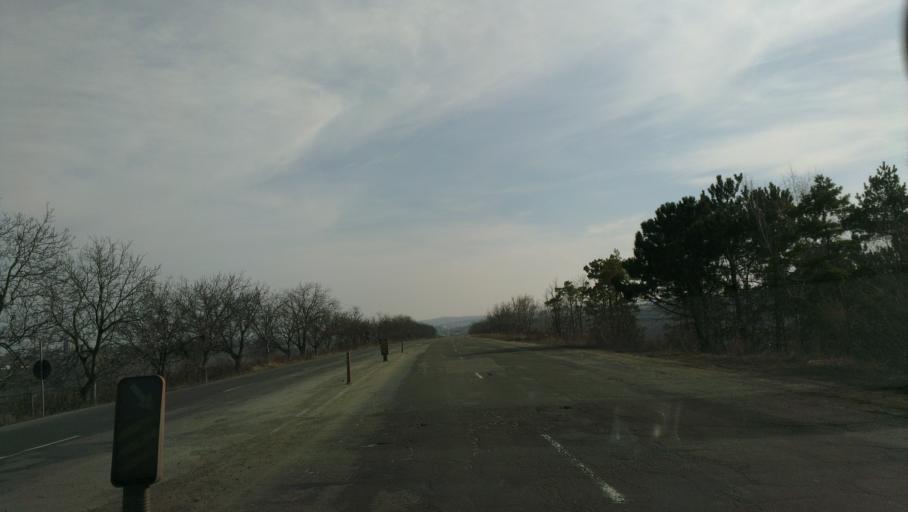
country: MD
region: Laloveni
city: Ialoveni
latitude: 46.9850
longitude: 28.7446
